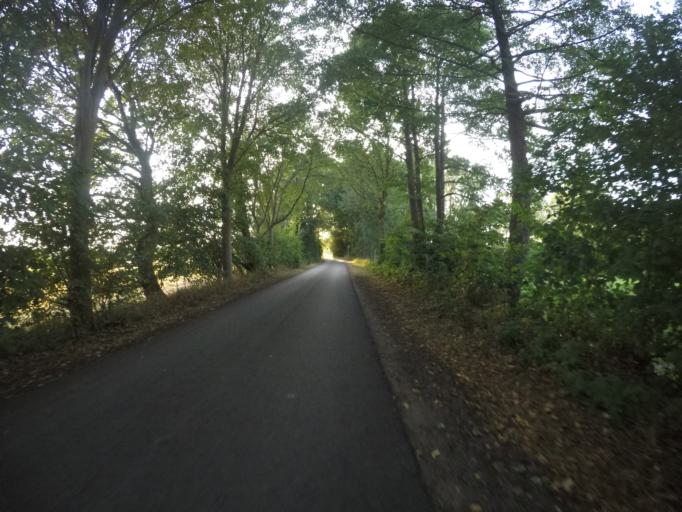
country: DE
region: North Rhine-Westphalia
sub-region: Regierungsbezirk Munster
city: Isselburg
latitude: 51.8510
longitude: 6.4859
